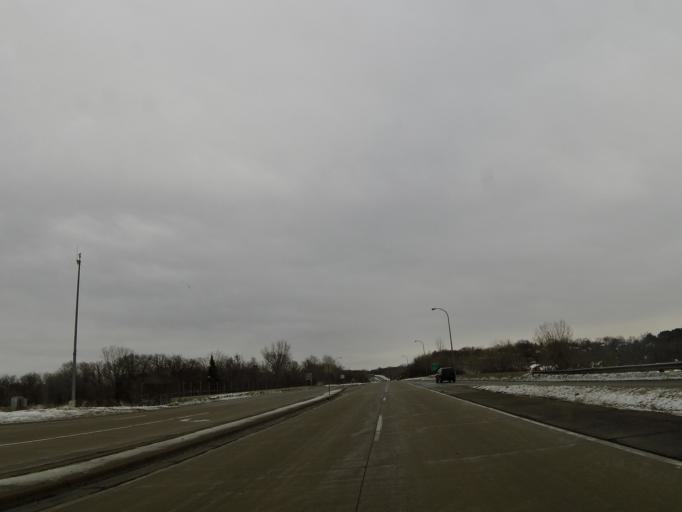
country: US
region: Minnesota
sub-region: Dakota County
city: Apple Valley
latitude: 44.7597
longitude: -93.2191
